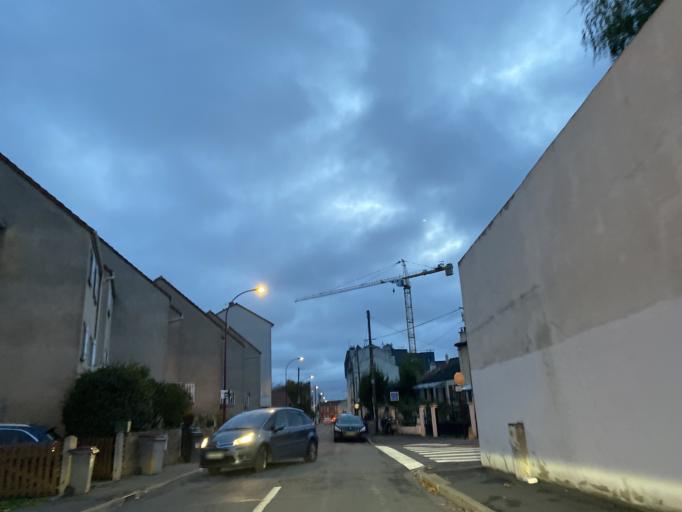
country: FR
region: Ile-de-France
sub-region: Departement du Val-d'Oise
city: Bezons
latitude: 48.9278
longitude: 2.2205
